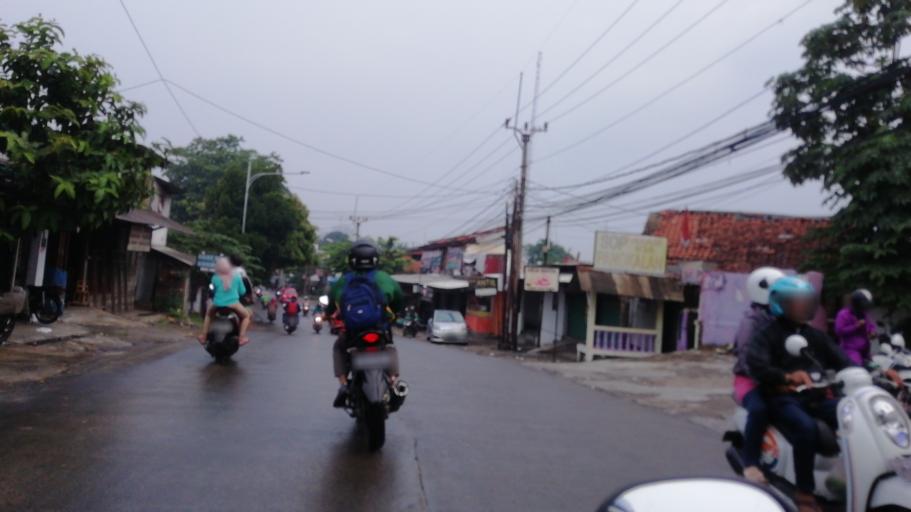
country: ID
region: West Java
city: Bogor
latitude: -6.5522
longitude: 106.8073
